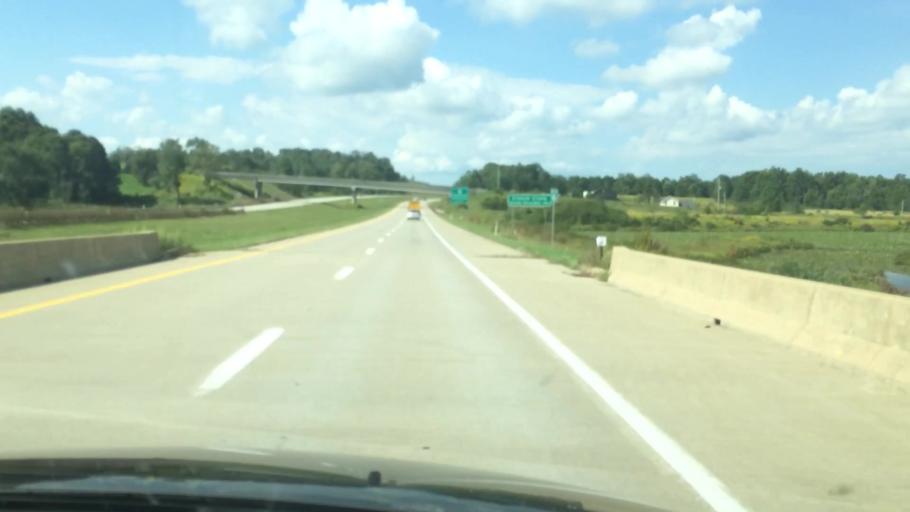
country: US
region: Pennsylvania
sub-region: Erie County
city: North East
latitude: 42.1272
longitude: -79.7796
